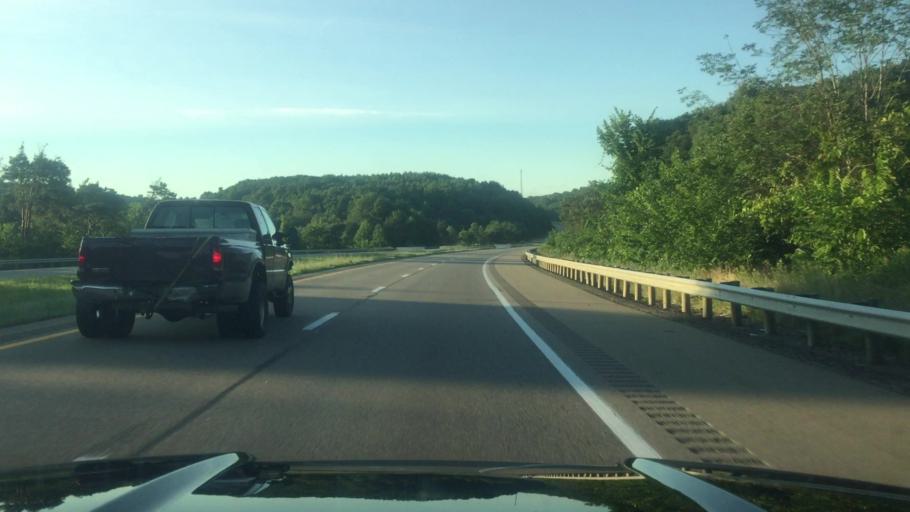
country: US
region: Ohio
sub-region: Tuscarawas County
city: Newcomerstown
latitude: 40.2318
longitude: -81.5542
